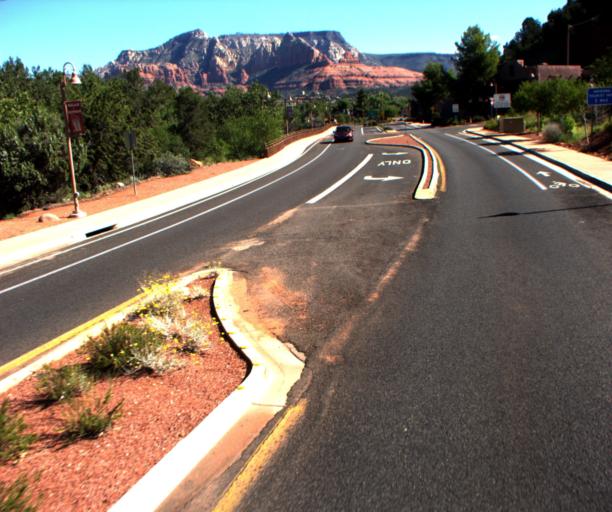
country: US
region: Arizona
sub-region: Coconino County
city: Sedona
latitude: 34.8599
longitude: -111.7623
